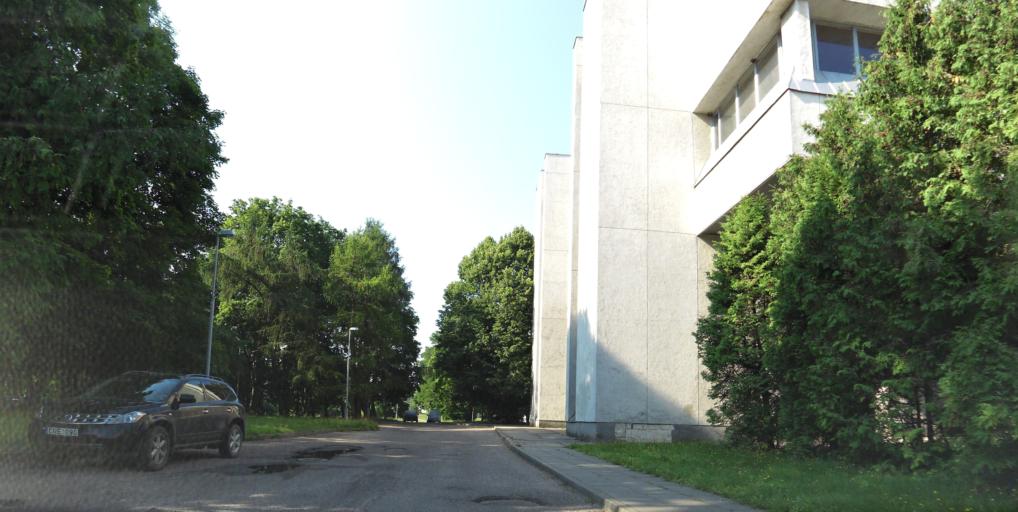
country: LT
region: Vilnius County
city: Rasos
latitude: 54.6967
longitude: 25.3014
